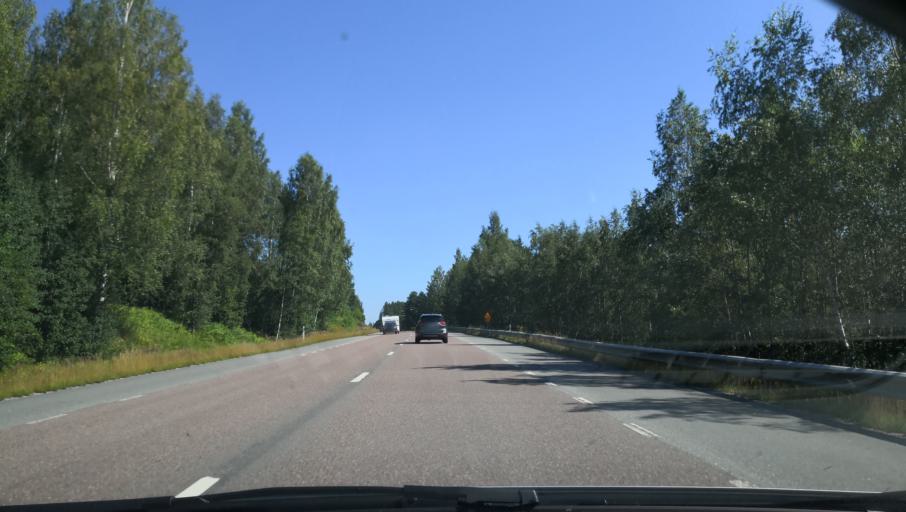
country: SE
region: Gaevleborg
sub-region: Bollnas Kommun
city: Bollnas
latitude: 61.3309
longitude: 16.2417
